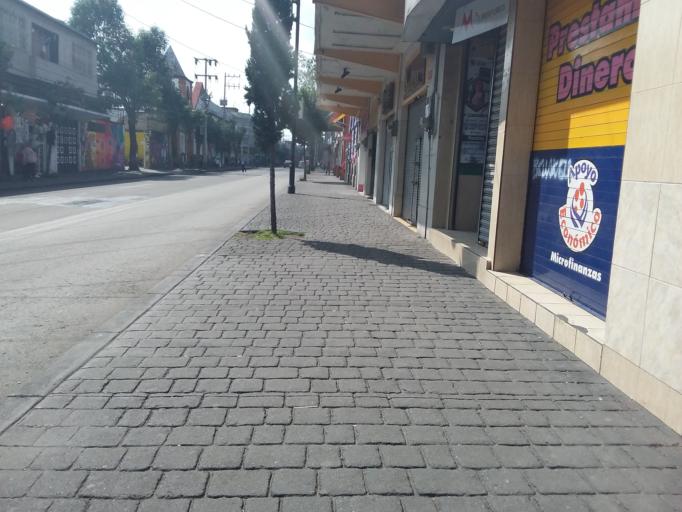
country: MX
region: Mexico
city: Toluca
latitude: 19.2917
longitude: -99.6544
